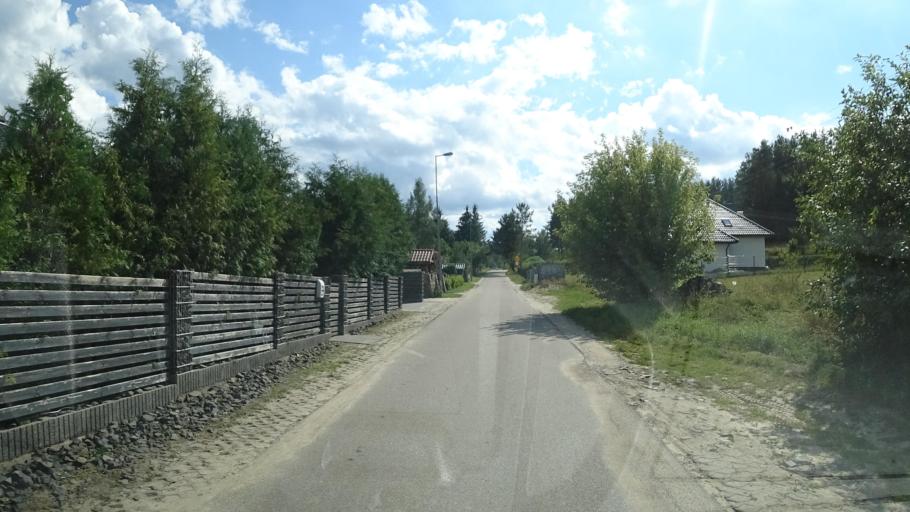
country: PL
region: Podlasie
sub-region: Powiat lomzynski
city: Piatnica
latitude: 53.1434
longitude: 22.1276
